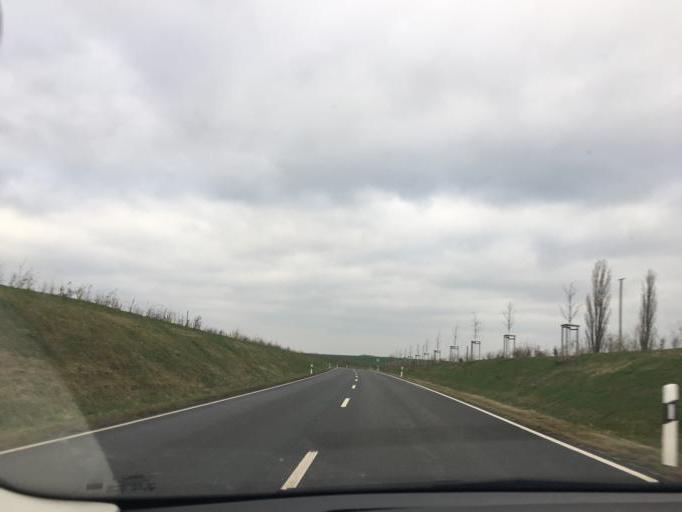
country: DE
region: Saxony
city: Niederfrohna
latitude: 50.8962
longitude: 12.7169
